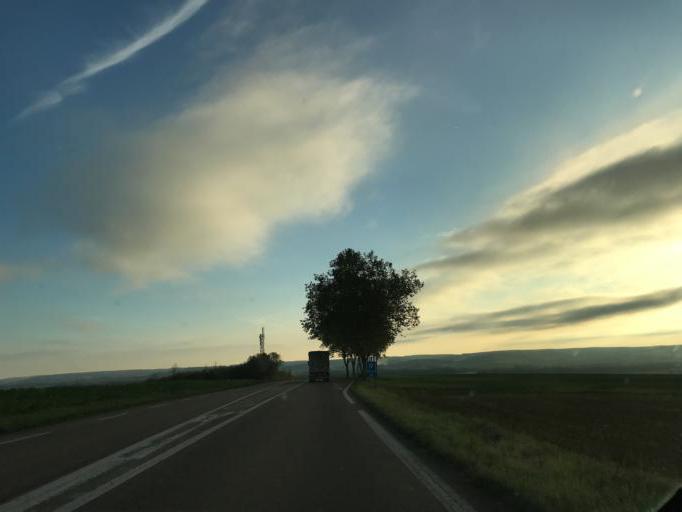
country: FR
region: Bourgogne
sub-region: Departement de l'Yonne
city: Sergines
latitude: 48.3326
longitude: 3.2304
